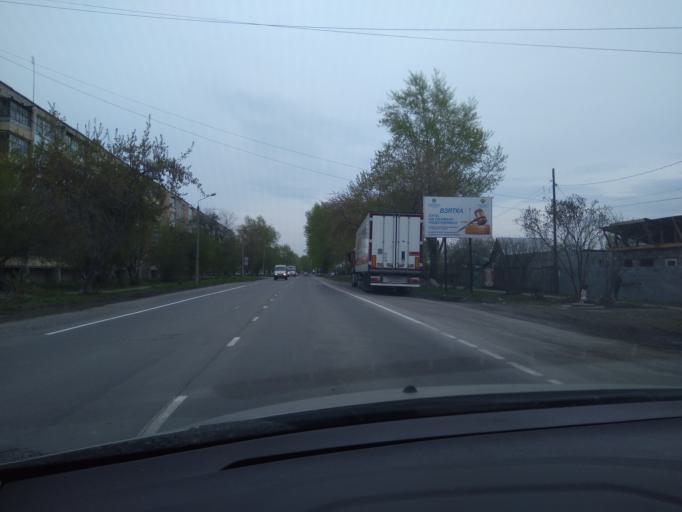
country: RU
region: Sverdlovsk
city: Bogdanovich
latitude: 56.7723
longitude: 62.0409
